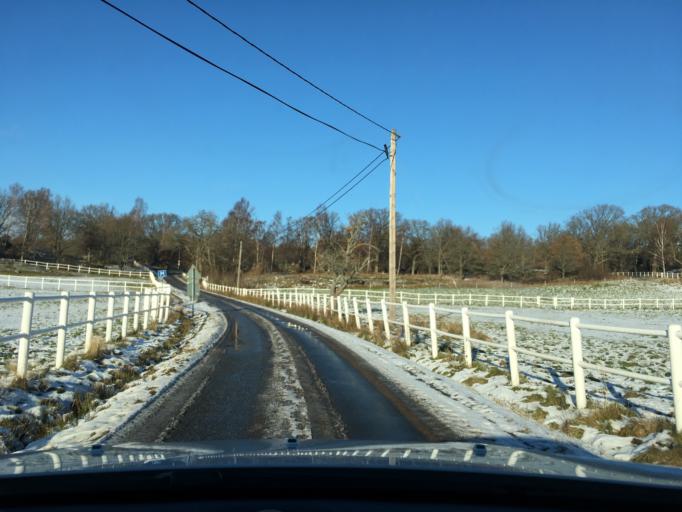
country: SE
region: Vaestra Goetaland
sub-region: Tjorns Kommun
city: Myggenas
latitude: 58.0948
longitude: 11.7700
